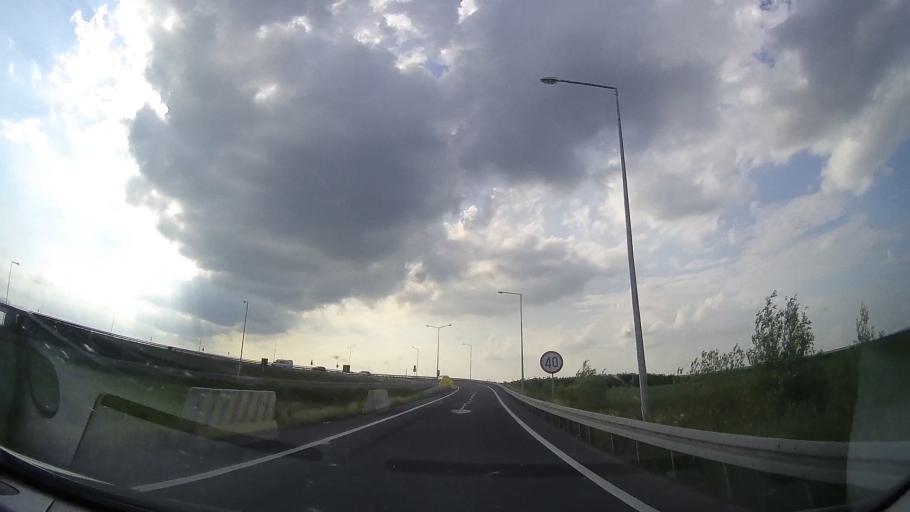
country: RO
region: Timis
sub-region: Comuna Remetea Mare
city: Remetea Mare
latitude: 45.8052
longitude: 21.4119
